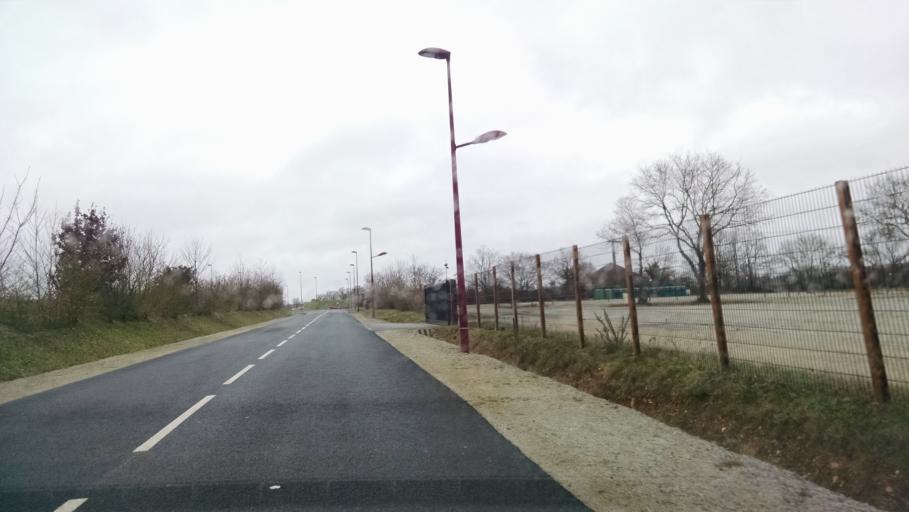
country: FR
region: Pays de la Loire
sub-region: Departement de la Loire-Atlantique
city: Clisson
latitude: 47.0960
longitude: -1.2689
